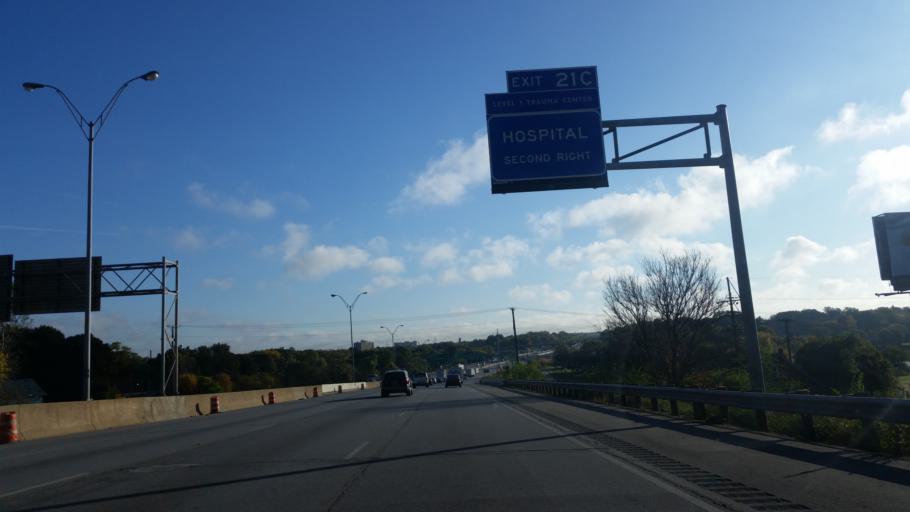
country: US
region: Ohio
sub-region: Summit County
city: Akron
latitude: 41.0607
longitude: -81.5519
